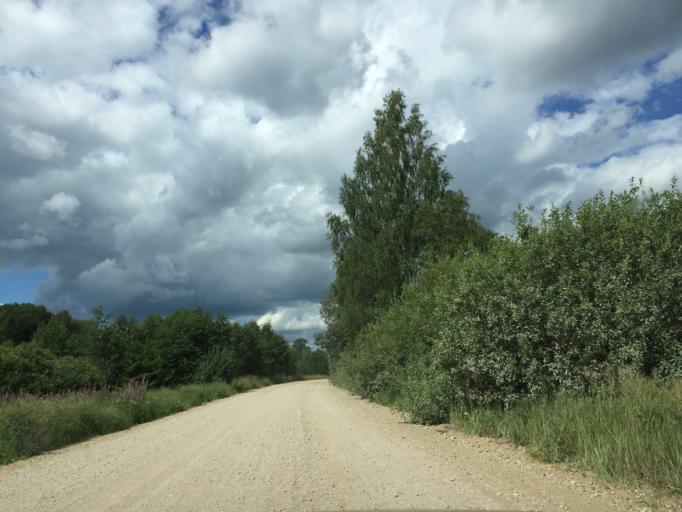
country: LV
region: Ropazu
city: Ropazi
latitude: 56.9057
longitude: 24.7804
